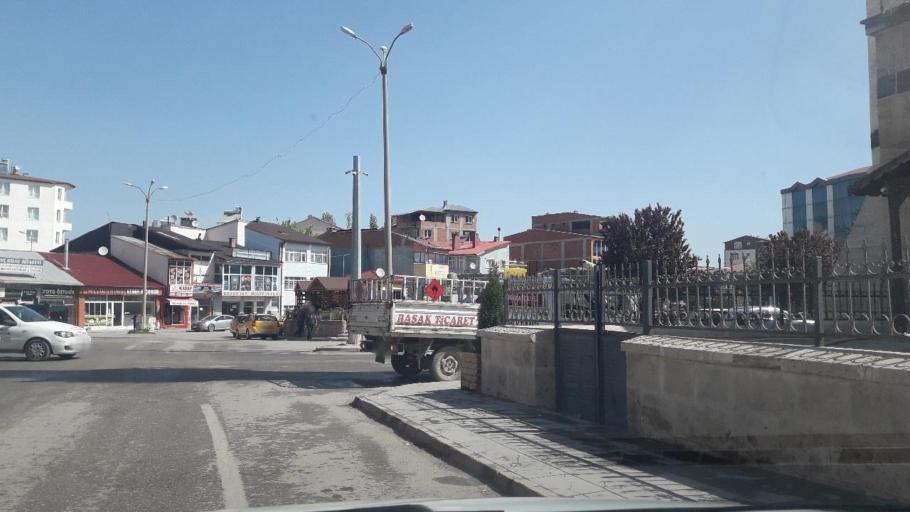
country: TR
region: Sivas
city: Kangal
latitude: 39.2354
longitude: 37.3911
